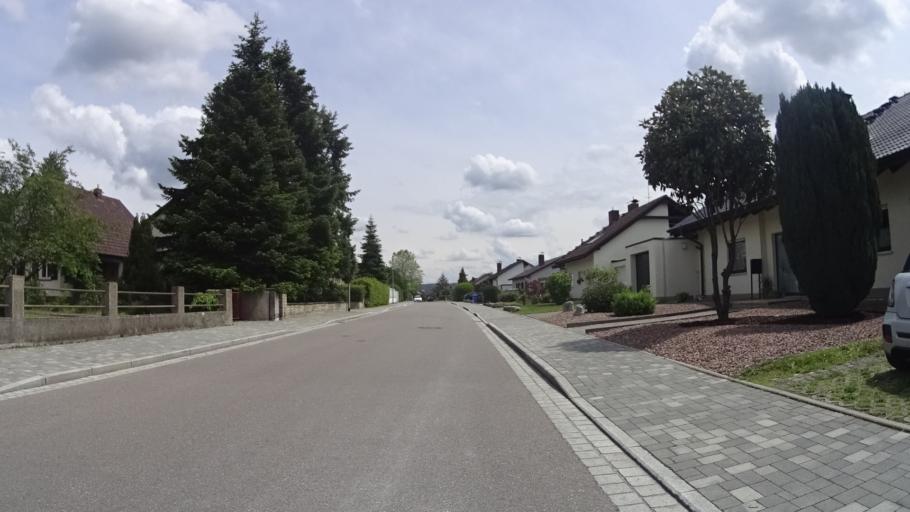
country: DE
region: Baden-Wuerttemberg
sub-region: Freiburg Region
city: Grenzach-Wyhlen
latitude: 47.5432
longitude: 7.6956
